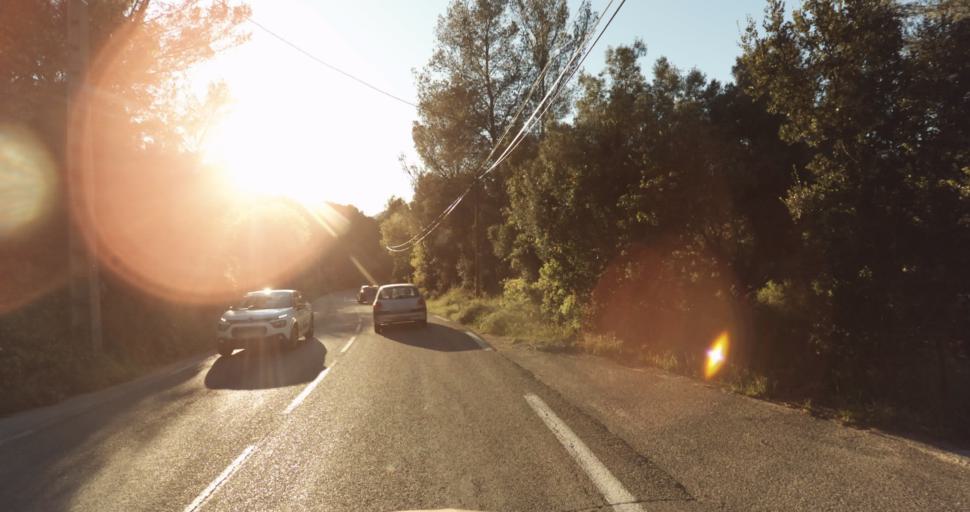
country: FR
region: Provence-Alpes-Cote d'Azur
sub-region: Departement du Var
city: La Valette-du-Var
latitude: 43.1576
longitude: 5.9578
